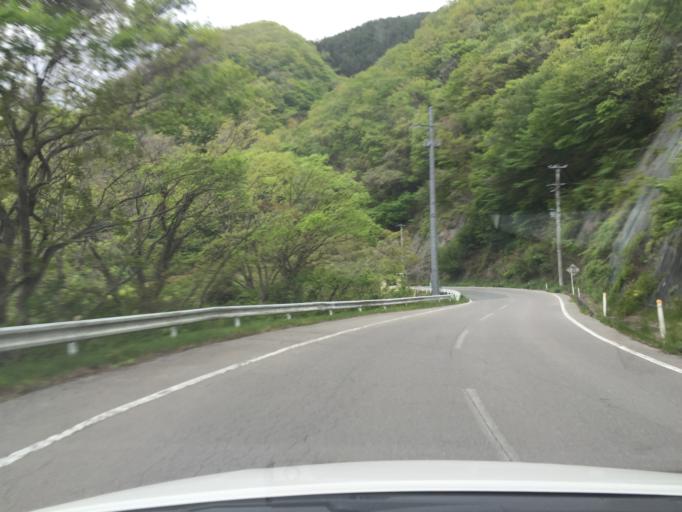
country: JP
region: Miyagi
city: Marumori
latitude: 37.7192
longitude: 140.8579
